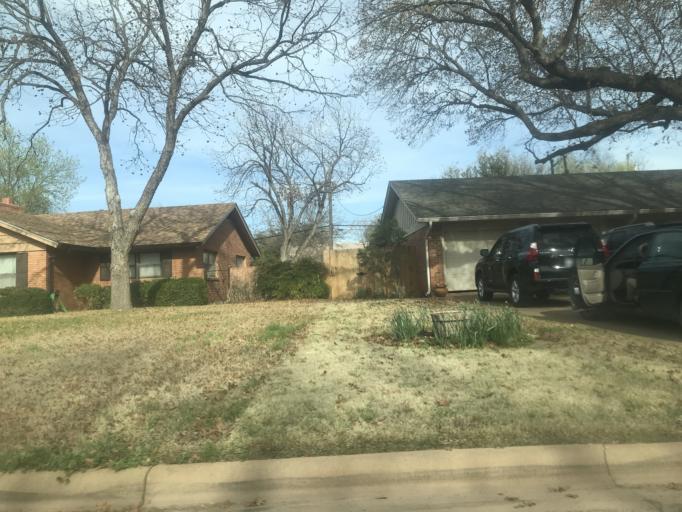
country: US
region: Texas
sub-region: Taylor County
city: Abilene
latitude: 32.4235
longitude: -99.7722
